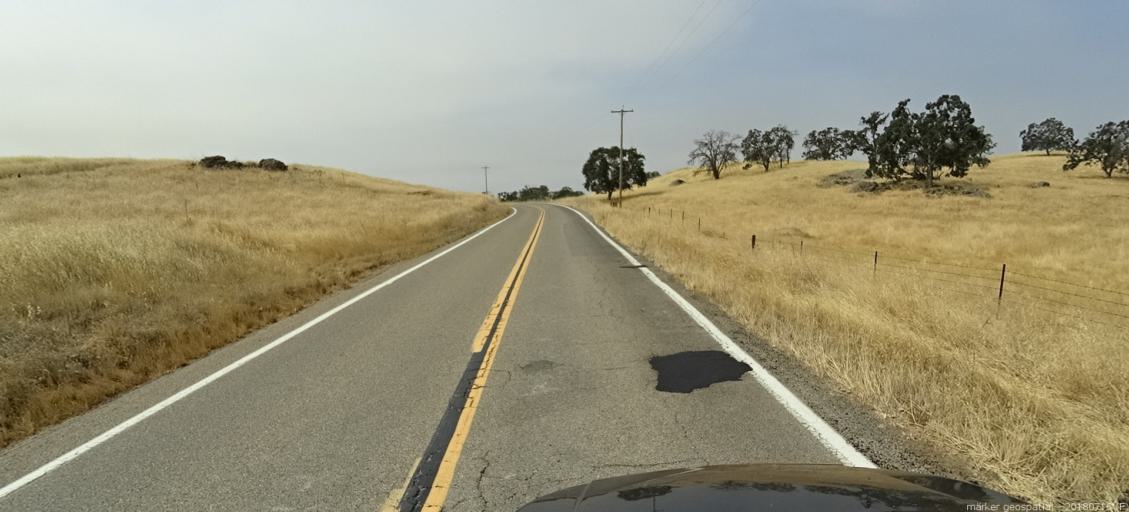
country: US
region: California
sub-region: Madera County
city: Yosemite Lakes
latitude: 37.1548
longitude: -119.9126
